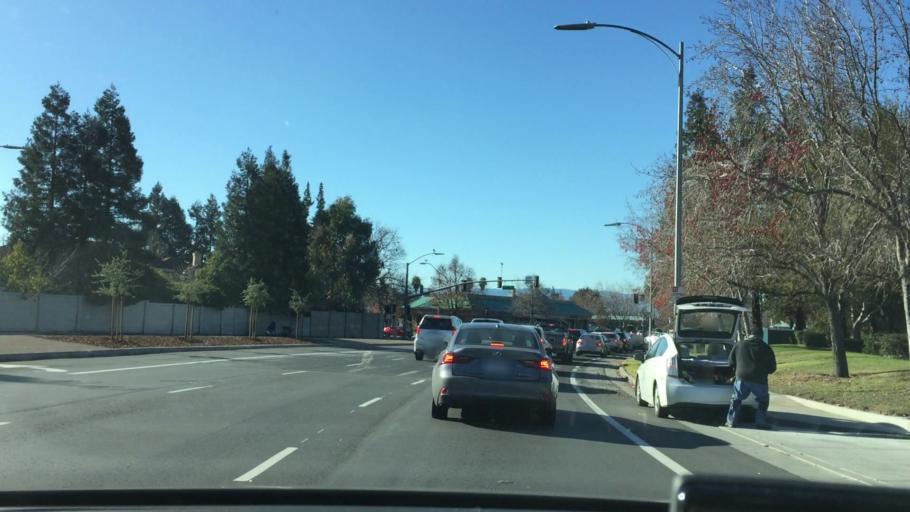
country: US
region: California
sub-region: Santa Clara County
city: Milpitas
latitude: 37.3887
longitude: -121.8816
